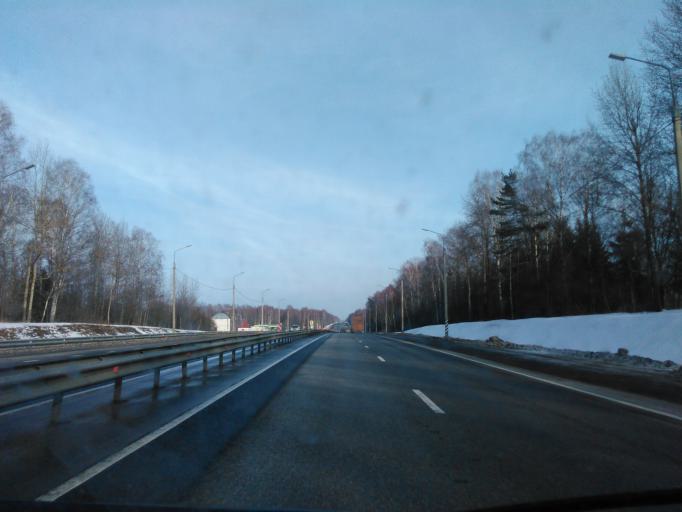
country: RU
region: Smolensk
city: Kholm-Zhirkovskiy
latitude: 55.1899
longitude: 33.7662
